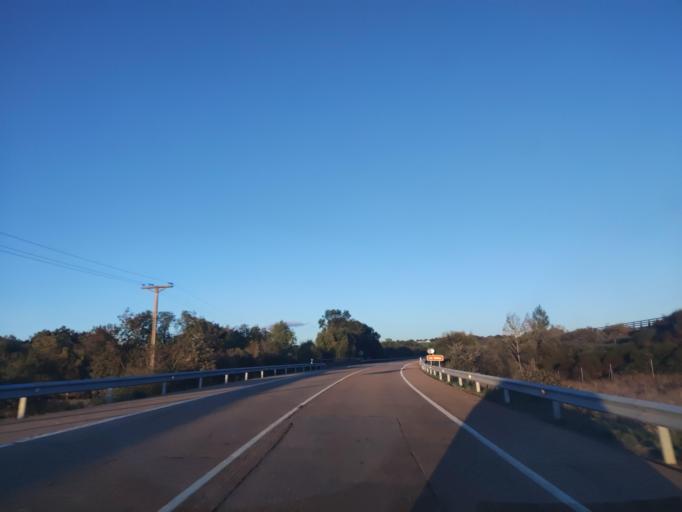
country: ES
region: Castille and Leon
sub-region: Provincia de Salamanca
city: Castraz
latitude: 40.7464
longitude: -6.3464
